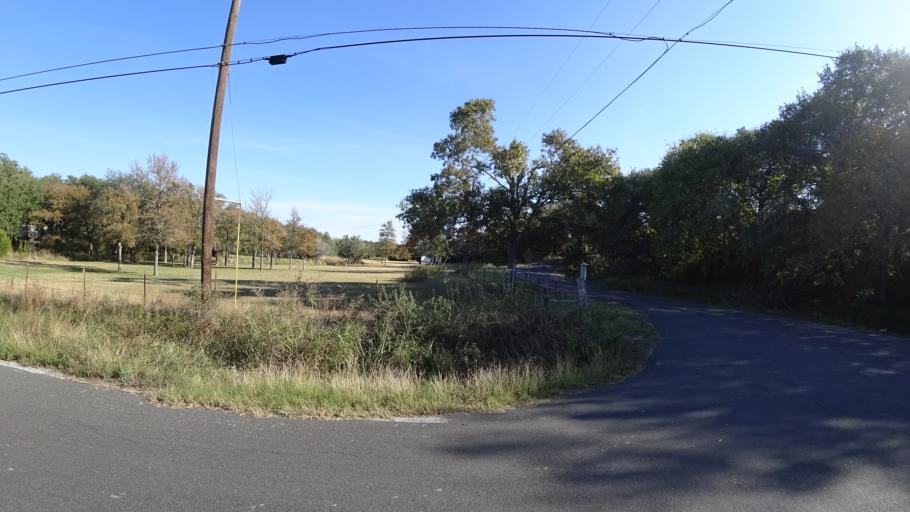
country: US
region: Texas
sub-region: Travis County
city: Barton Creek
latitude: 30.2351
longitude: -97.9260
